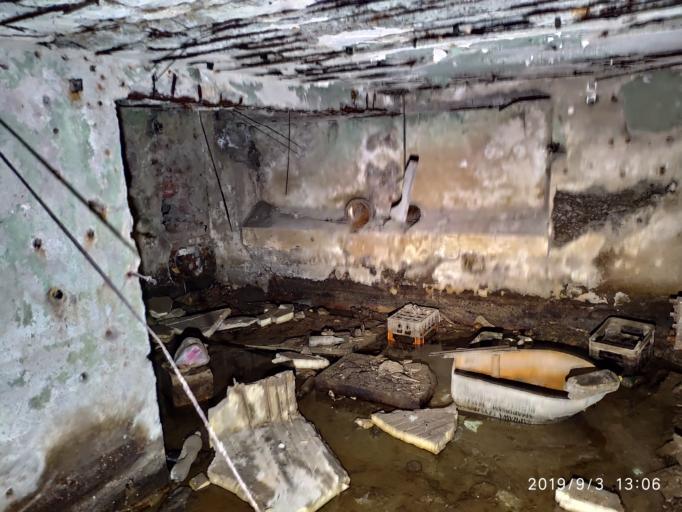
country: PL
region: Lubusz
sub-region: Powiat nowosolski
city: Nowa Sol
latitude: 51.7949
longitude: 15.7148
